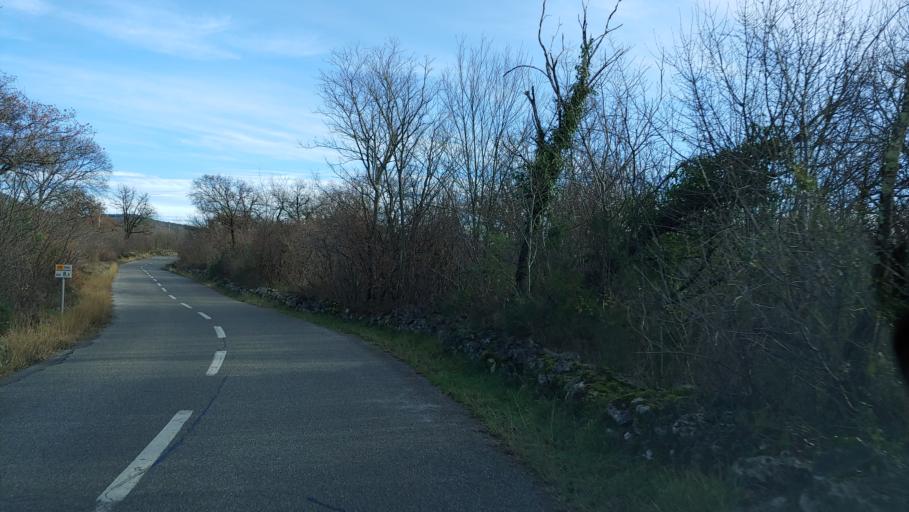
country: IT
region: Friuli Venezia Giulia
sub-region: Provincia di Trieste
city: Duino
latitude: 45.8120
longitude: 13.6146
